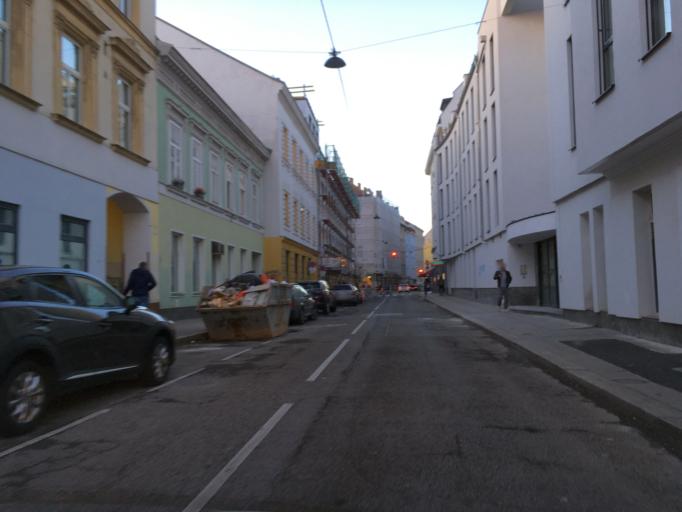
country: AT
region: Vienna
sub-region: Wien Stadt
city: Vienna
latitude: 48.1868
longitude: 16.3314
